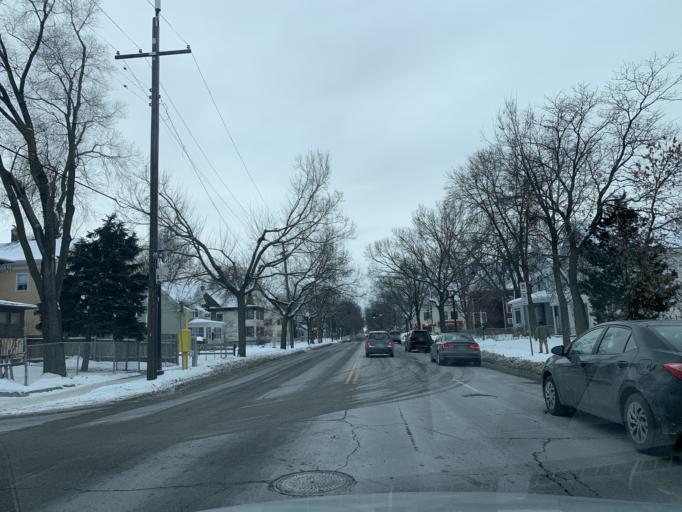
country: US
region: Minnesota
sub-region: Hennepin County
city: Minneapolis
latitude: 44.9566
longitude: -93.2474
